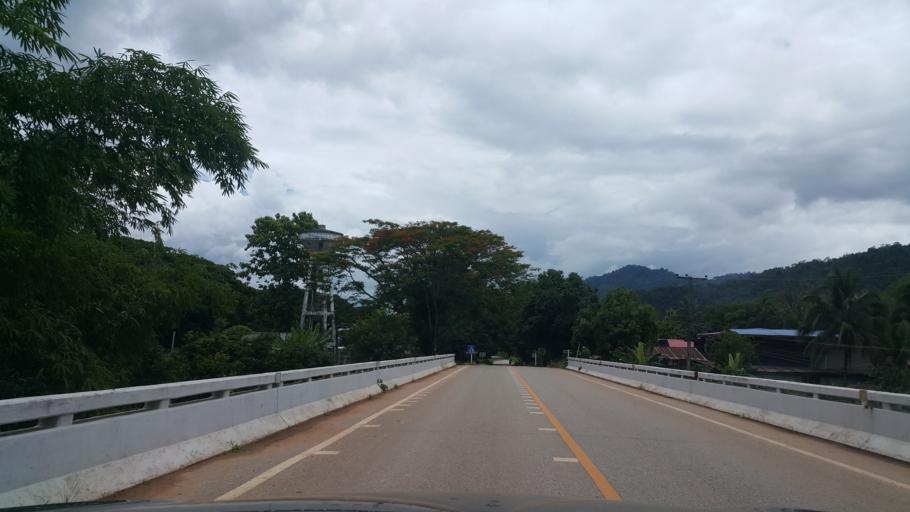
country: TH
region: Phitsanulok
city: Chat Trakan
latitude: 17.3856
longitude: 100.7556
